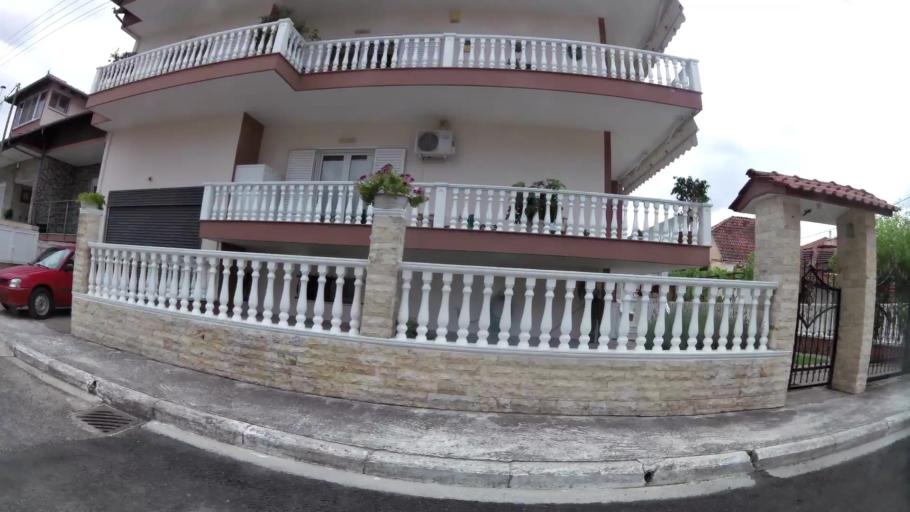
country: GR
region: Central Macedonia
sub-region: Nomos Pierias
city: Kallithea
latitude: 40.2723
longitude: 22.5746
